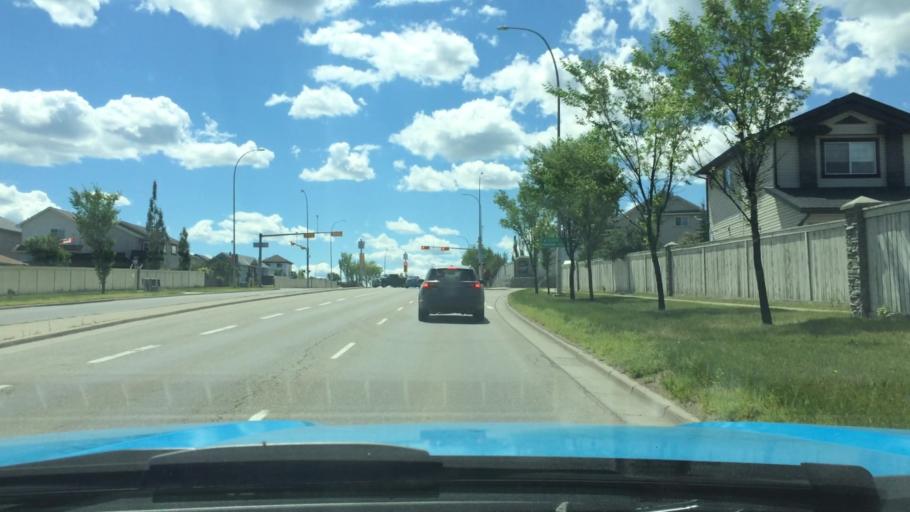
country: CA
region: Alberta
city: Calgary
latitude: 51.1523
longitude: -114.0681
